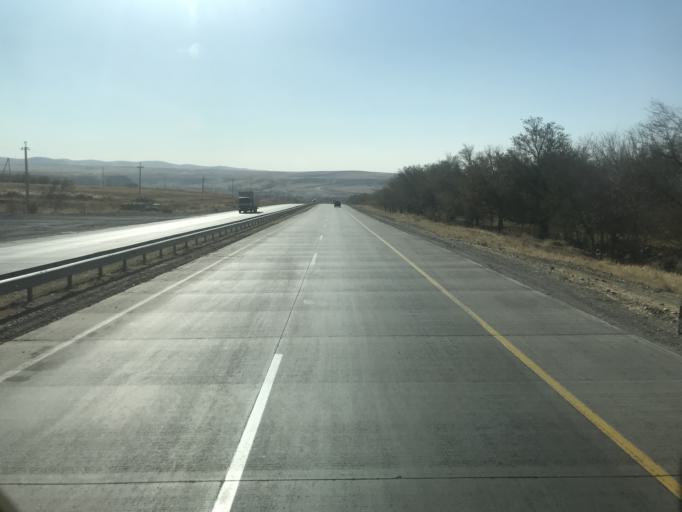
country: KZ
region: Ongtustik Qazaqstan
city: Sastobe
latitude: 42.5141
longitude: 69.9840
